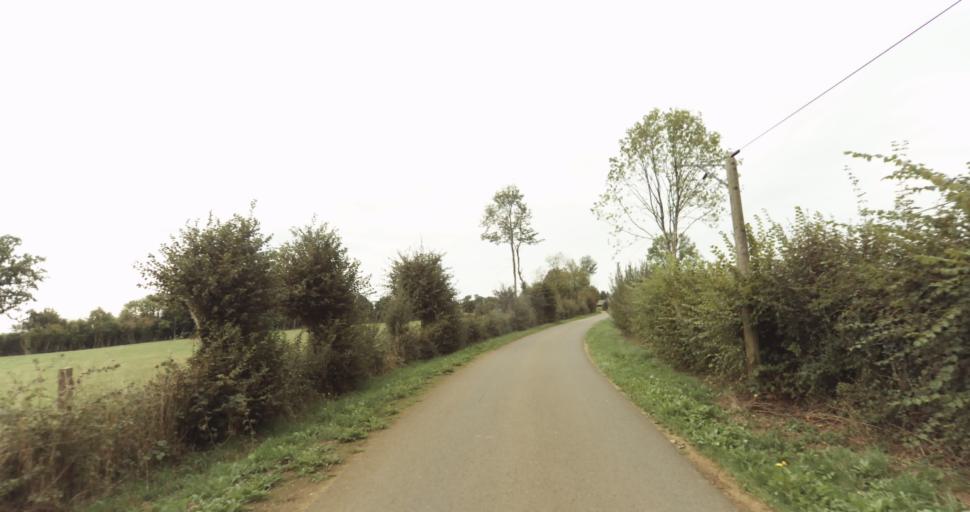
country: FR
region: Lower Normandy
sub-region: Departement de l'Orne
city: Gace
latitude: 48.7305
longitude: 0.3294
